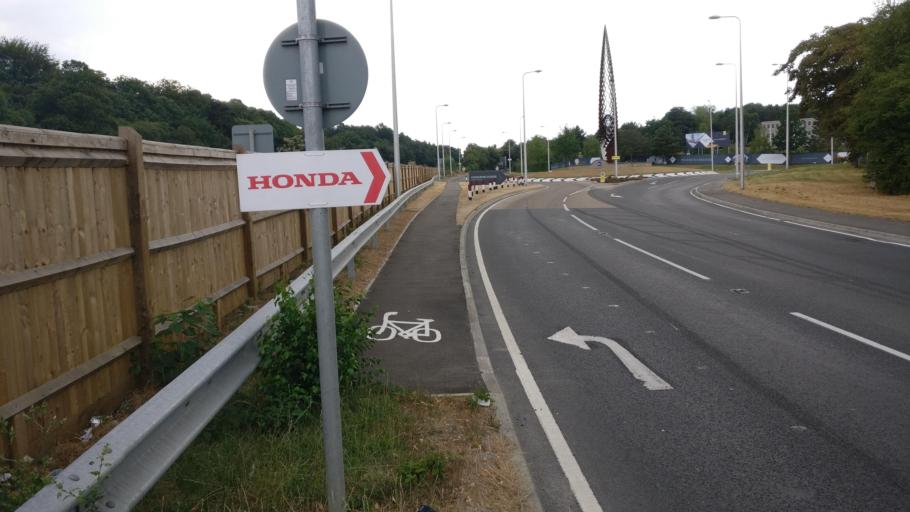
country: GB
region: England
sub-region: Surrey
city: Virginia Water
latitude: 51.3810
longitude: -0.5913
